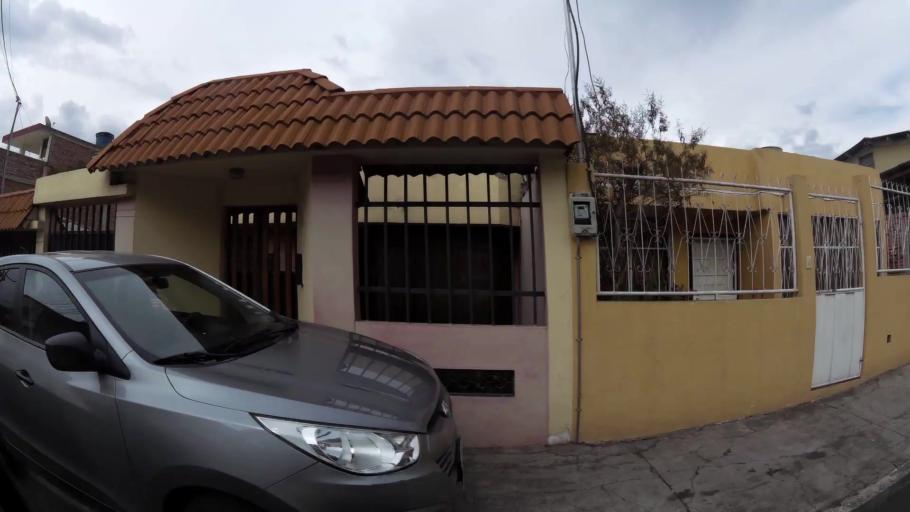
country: EC
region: Tungurahua
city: Ambato
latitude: -1.2600
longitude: -78.6385
